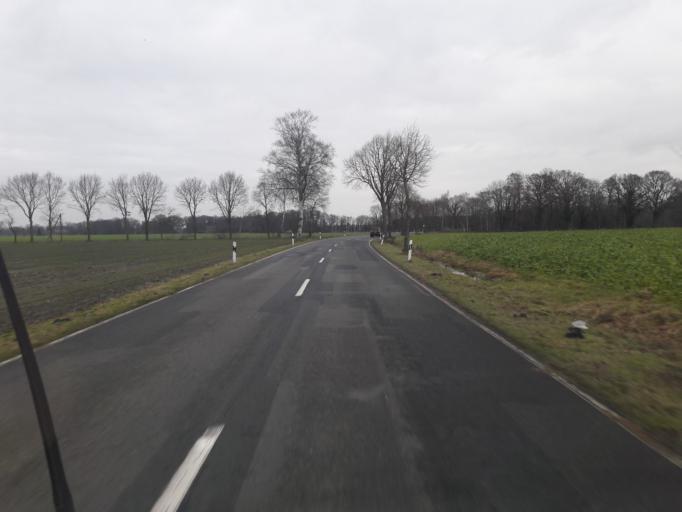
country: DE
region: Lower Saxony
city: Warmsen
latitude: 52.4024
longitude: 8.8596
